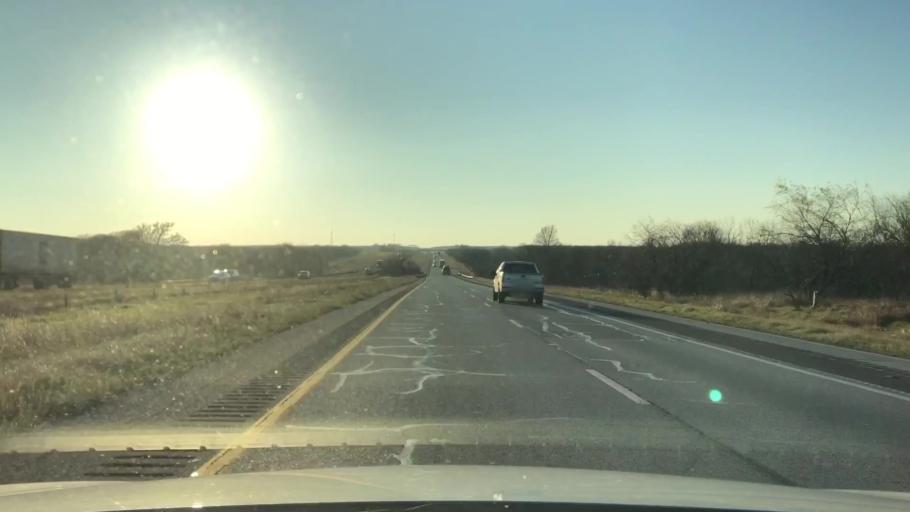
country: US
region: Texas
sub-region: Caldwell County
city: Luling
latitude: 29.6325
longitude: -97.7406
